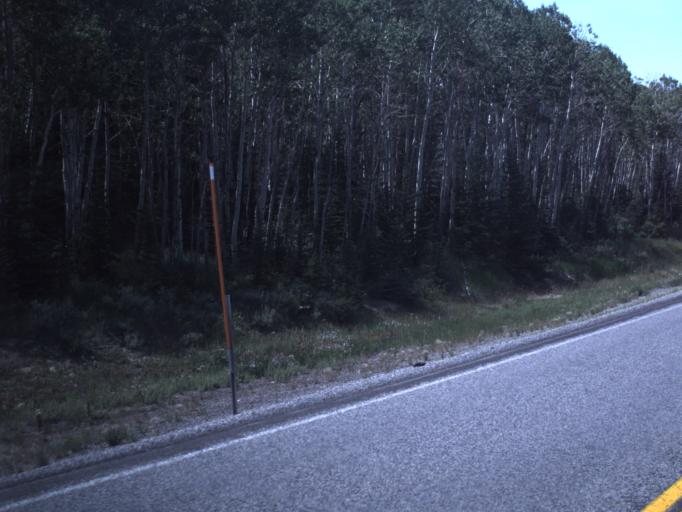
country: US
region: Utah
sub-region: Carbon County
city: Helper
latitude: 39.8647
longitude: -111.1181
